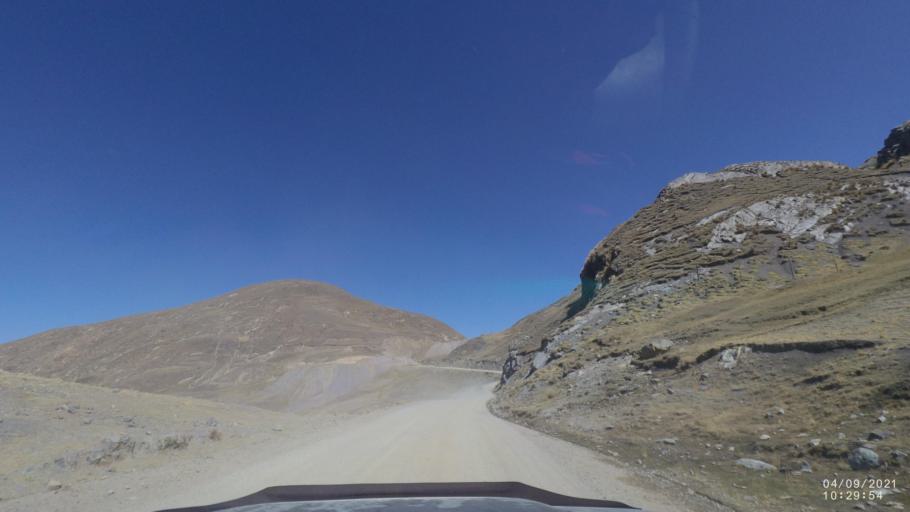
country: BO
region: Cochabamba
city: Sipe Sipe
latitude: -17.3027
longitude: -66.4404
